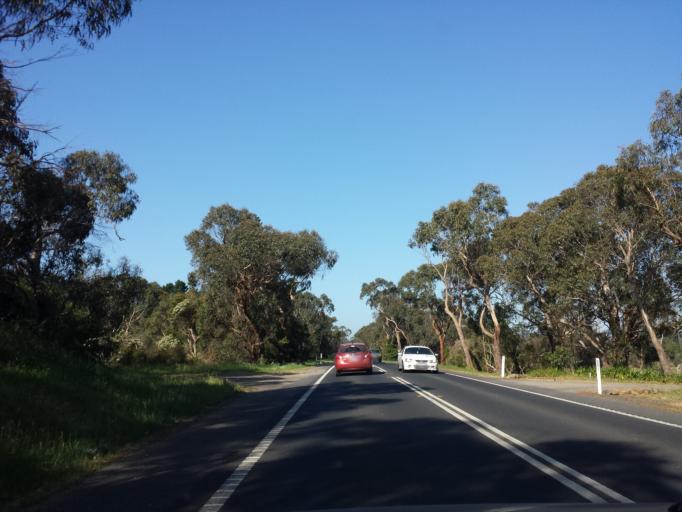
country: AU
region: Victoria
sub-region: Casey
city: Narre Warren North
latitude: -37.9644
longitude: 145.3346
